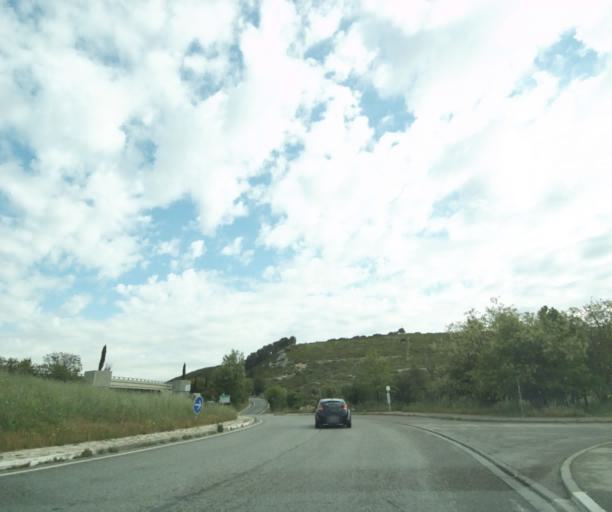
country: FR
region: Provence-Alpes-Cote d'Azur
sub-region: Departement des Bouches-du-Rhone
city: Cabries
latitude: 43.4784
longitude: 5.3561
